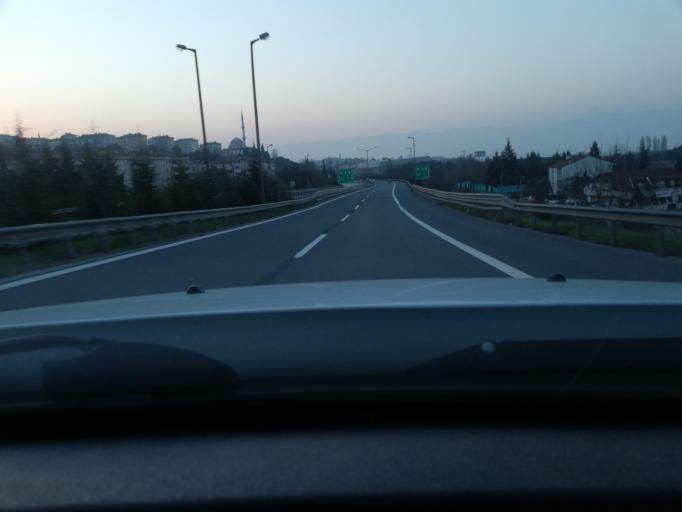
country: TR
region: Kocaeli
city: Derince
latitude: 40.7663
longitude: 29.8538
